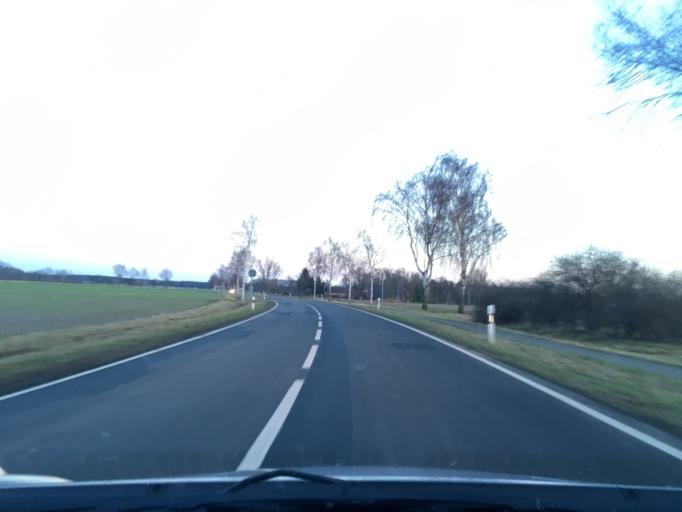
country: DE
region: Lower Saxony
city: Waddeweitz
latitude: 52.9872
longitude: 10.9828
